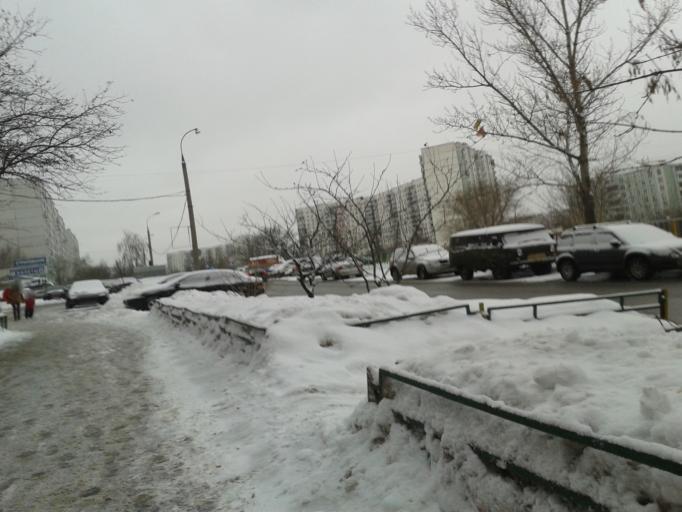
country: RU
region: Moscow
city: Strogino
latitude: 55.8063
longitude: 37.4082
